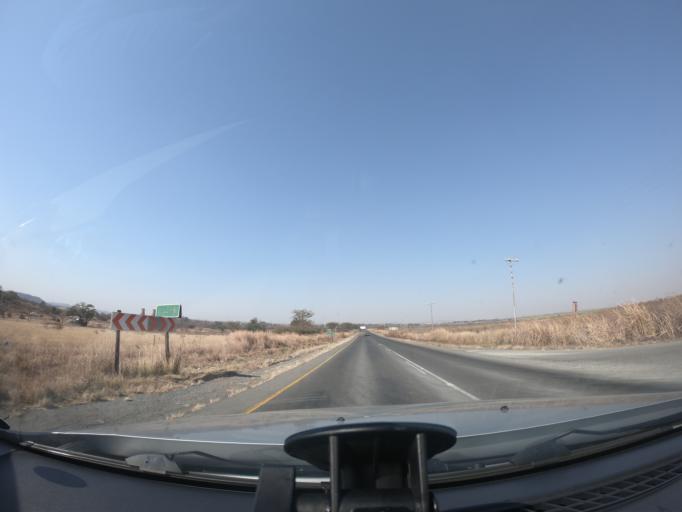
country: ZA
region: KwaZulu-Natal
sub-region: uThukela District Municipality
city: Ladysmith
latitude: -28.7294
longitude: 29.8102
